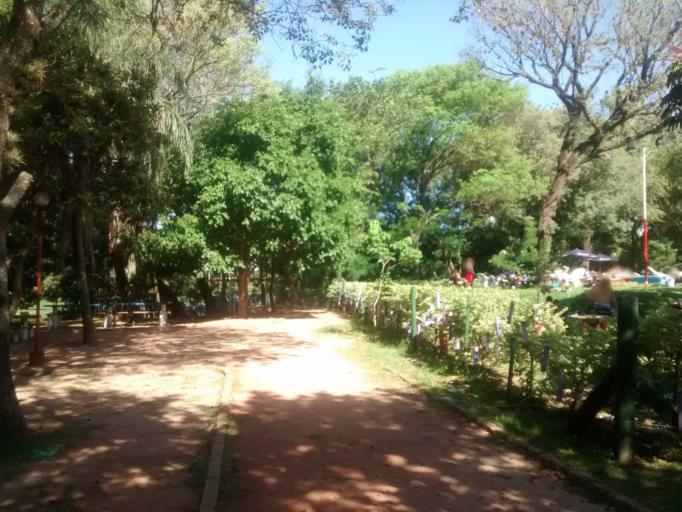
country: AR
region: Chaco
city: Resistencia
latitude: -27.4351
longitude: -58.9852
